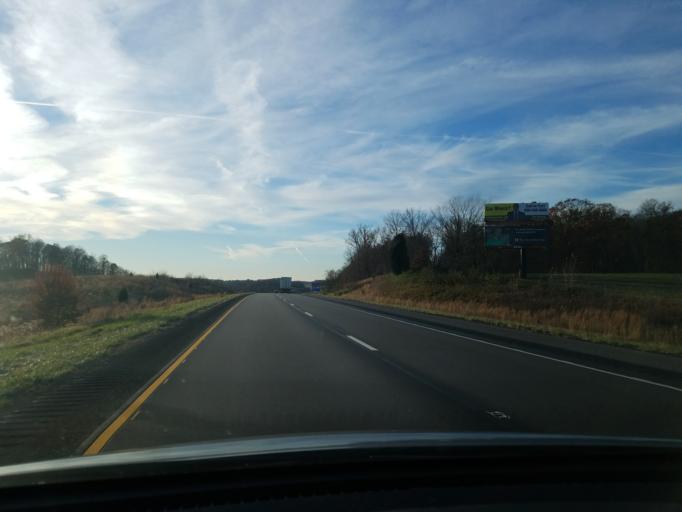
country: US
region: Indiana
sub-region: Dubois County
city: Ferdinand
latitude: 38.2027
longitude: -86.8307
